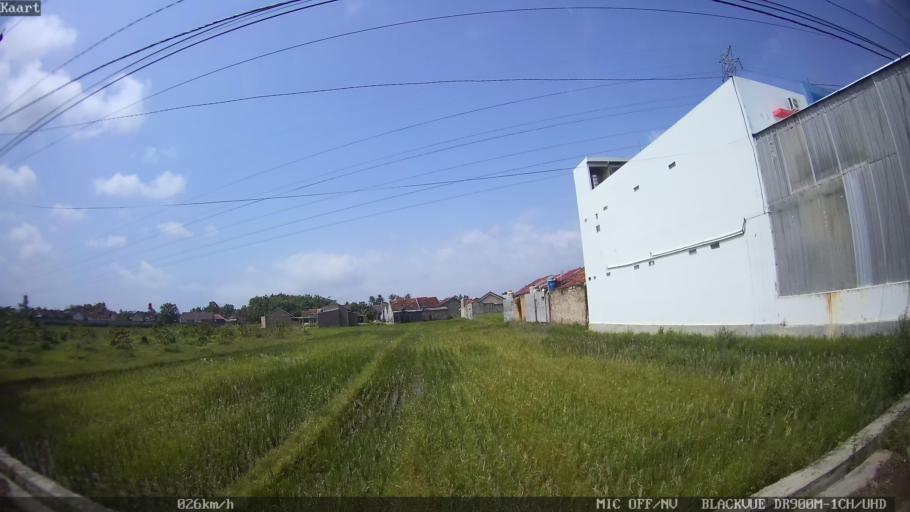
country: ID
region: Lampung
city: Kedaton
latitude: -5.3484
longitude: 105.2791
